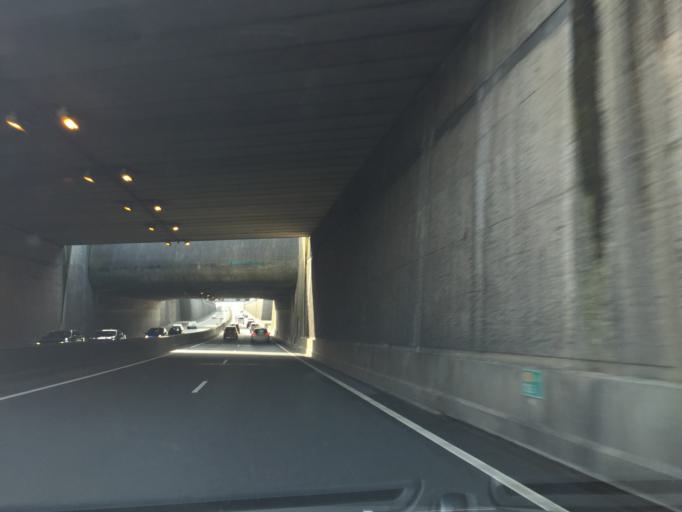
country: NL
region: South Holland
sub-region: Gemeente Alphen aan den Rijn
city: Alphen aan den Rijn
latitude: 52.1116
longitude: 4.6717
